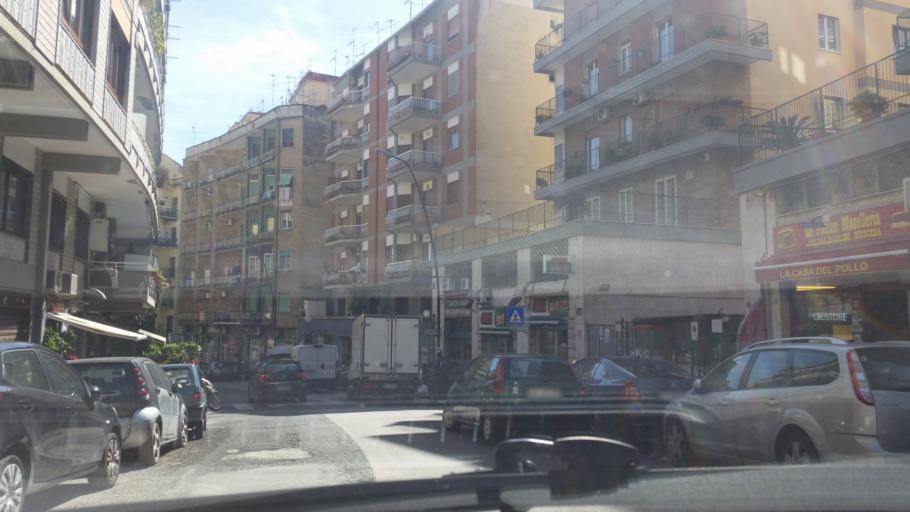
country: IT
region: Campania
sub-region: Provincia di Napoli
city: Napoli
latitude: 40.8532
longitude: 14.2356
